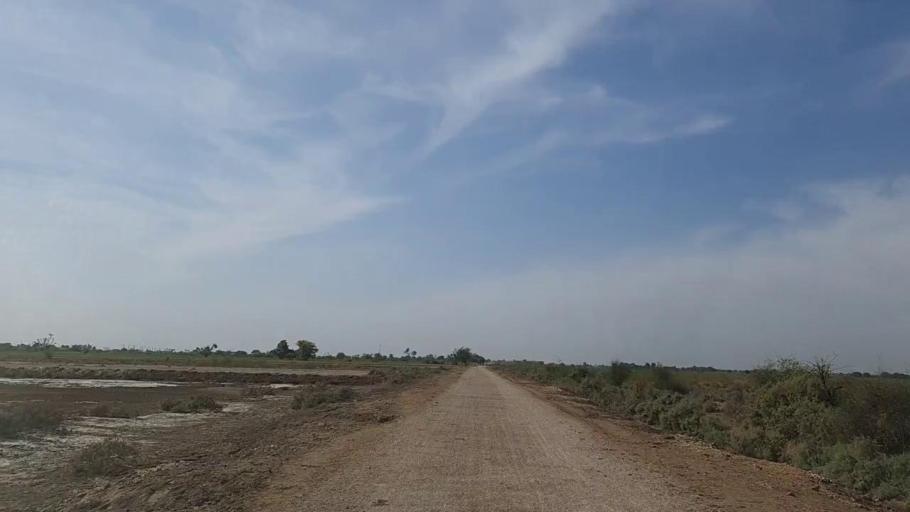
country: PK
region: Sindh
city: Samaro
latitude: 25.2080
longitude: 69.4422
